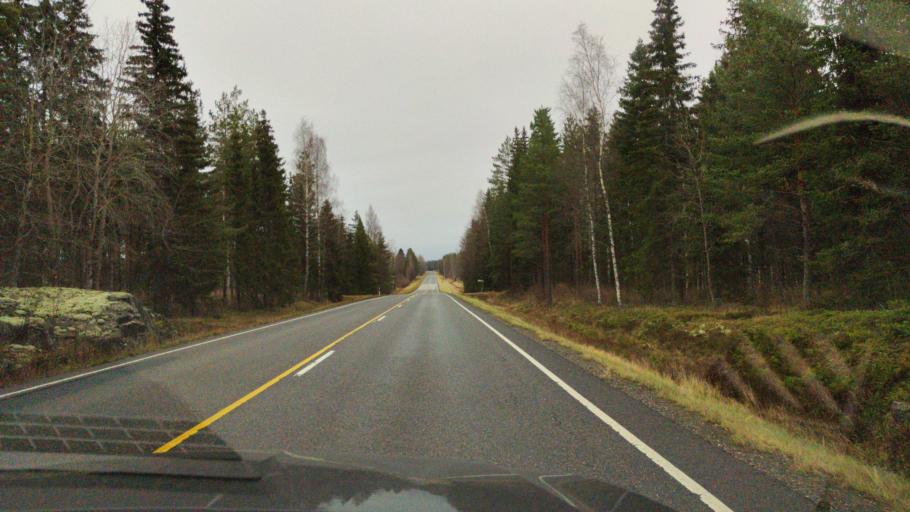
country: FI
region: Varsinais-Suomi
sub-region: Loimaa
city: Ylaene
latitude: 60.7721
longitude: 22.4391
